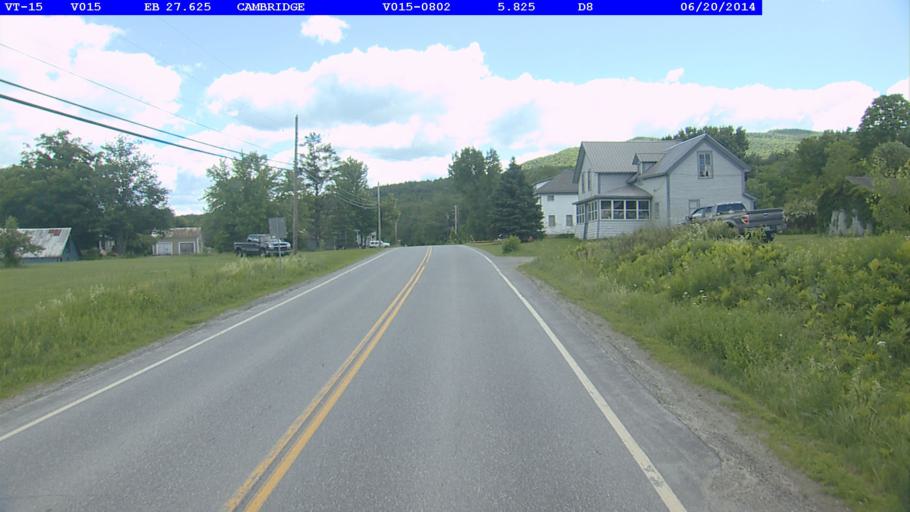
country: US
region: Vermont
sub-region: Lamoille County
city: Johnson
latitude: 44.6496
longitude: -72.8160
